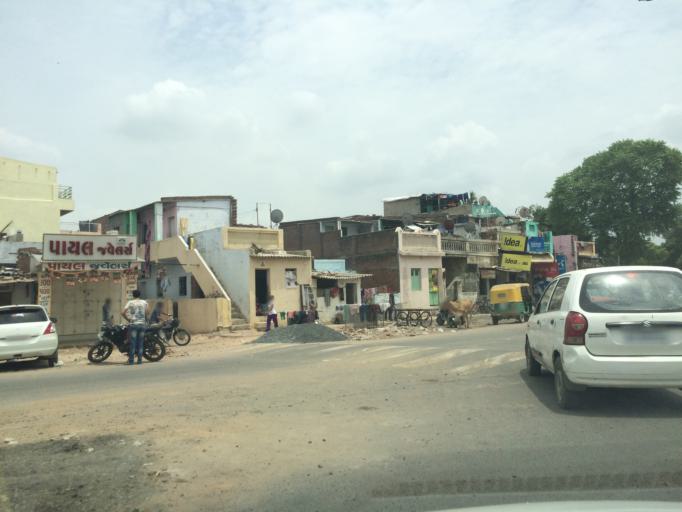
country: IN
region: Gujarat
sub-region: Ahmadabad
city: Ahmedabad
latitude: 23.0729
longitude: 72.5652
